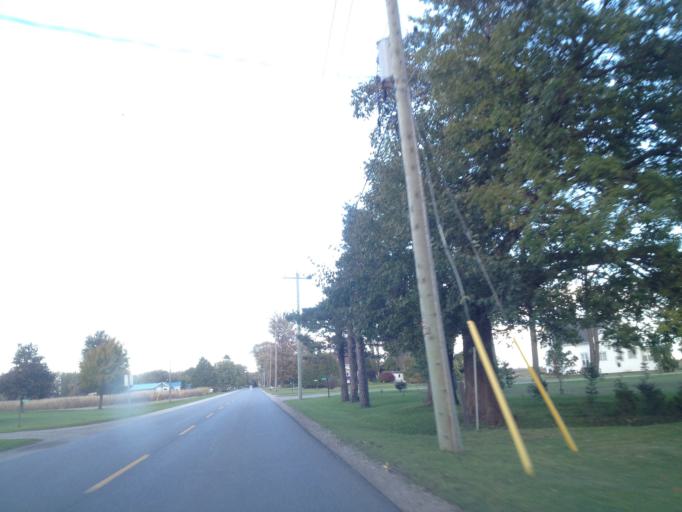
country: CA
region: Ontario
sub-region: Lambton County
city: Walpole Island
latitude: 42.3115
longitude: -82.4266
